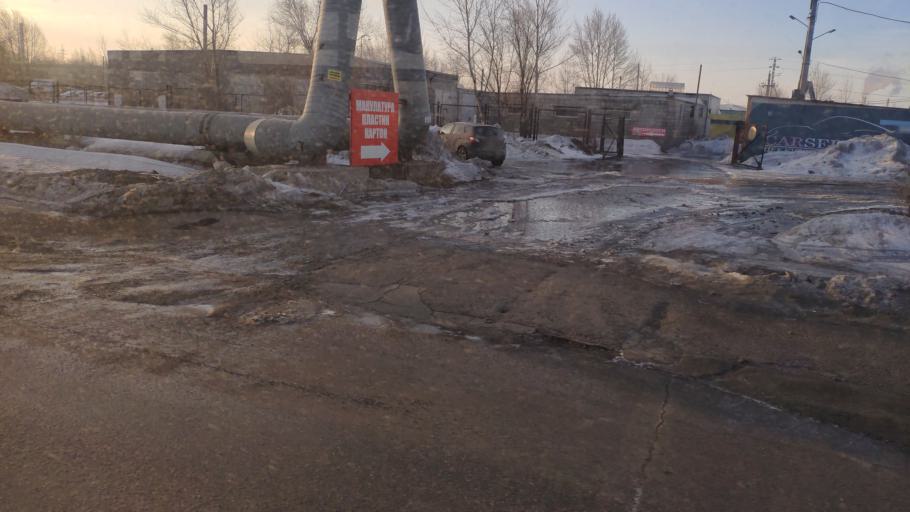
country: RU
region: Chelyabinsk
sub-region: Gorod Magnitogorsk
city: Magnitogorsk
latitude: 53.4222
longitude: 59.0254
